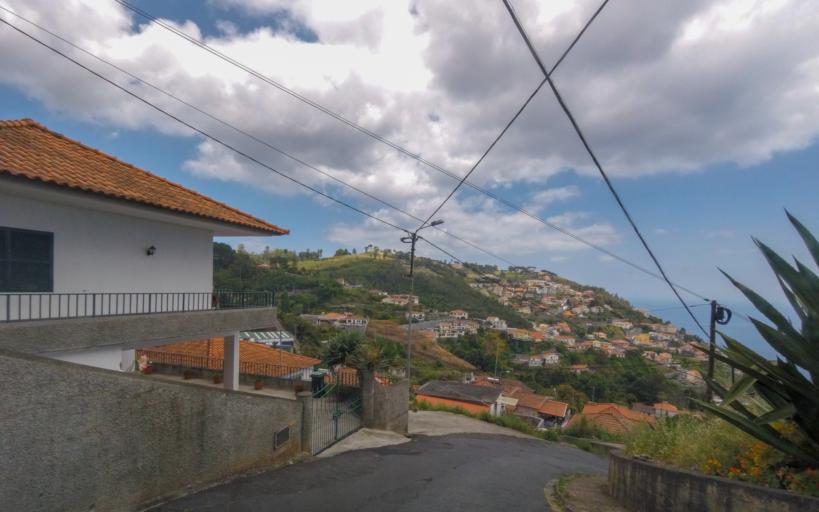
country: PT
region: Madeira
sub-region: Funchal
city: Nossa Senhora do Monte
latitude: 32.6622
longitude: -16.8785
